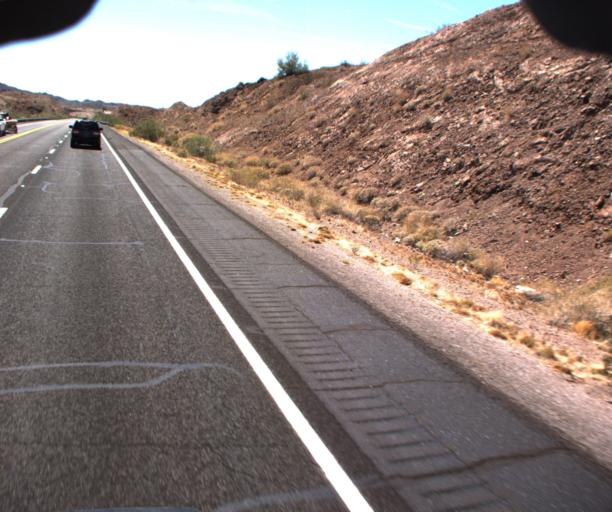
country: US
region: Arizona
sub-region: La Paz County
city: Cienega Springs
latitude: 34.2346
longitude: -114.1784
